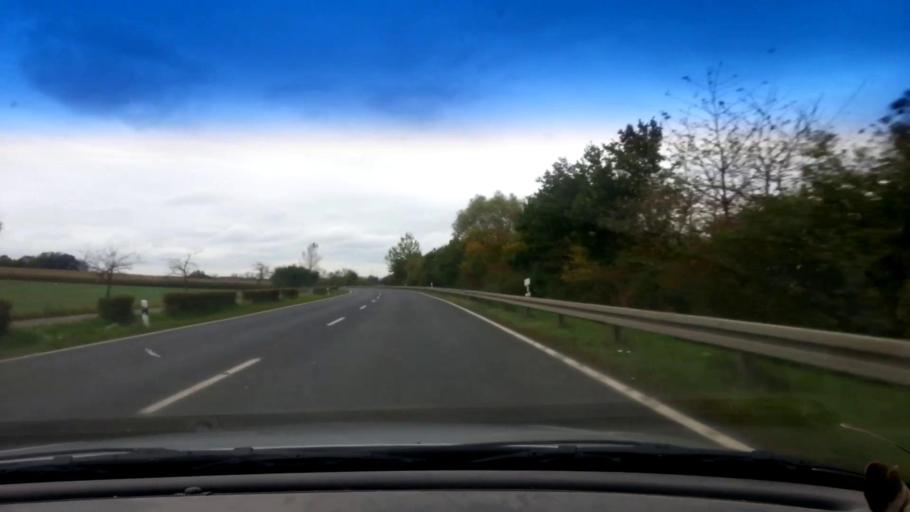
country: DE
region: Bavaria
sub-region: Upper Franconia
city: Baunach
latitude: 49.9991
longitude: 10.8403
